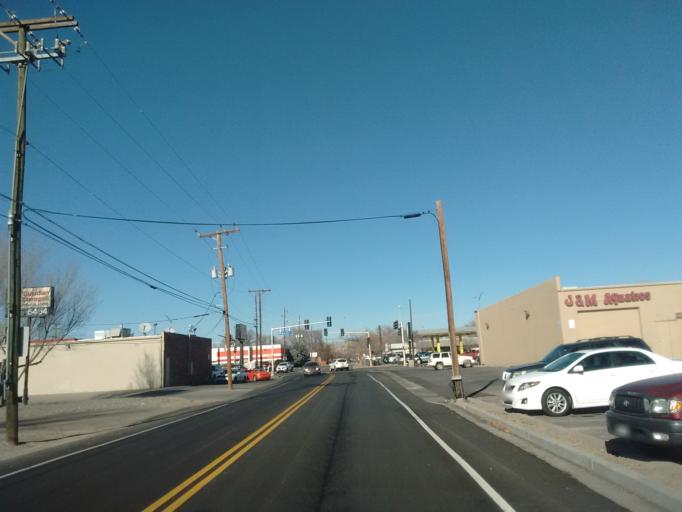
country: US
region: Colorado
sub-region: Mesa County
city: Fruitvale
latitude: 39.0766
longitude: -108.5244
